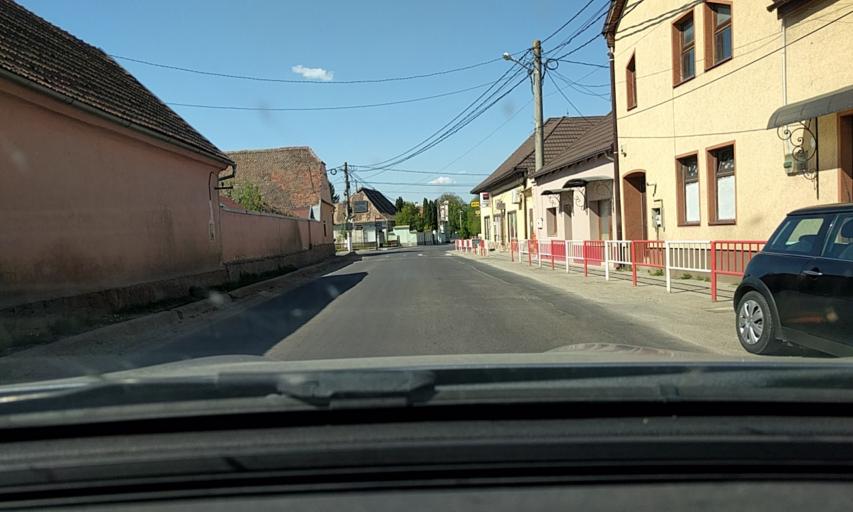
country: RO
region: Brasov
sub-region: Comuna Harman
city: Harman
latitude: 45.7131
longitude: 25.6845
